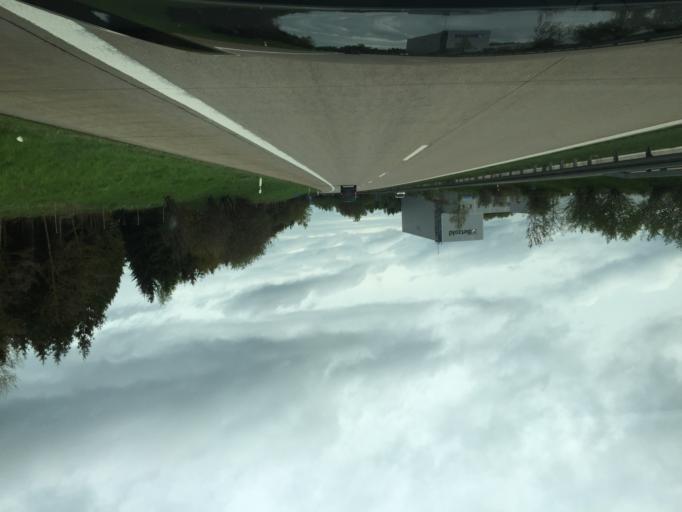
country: DE
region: Baden-Wuerttemberg
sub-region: Regierungsbezirk Stuttgart
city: Ellwangen
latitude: 48.9597
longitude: 10.1851
